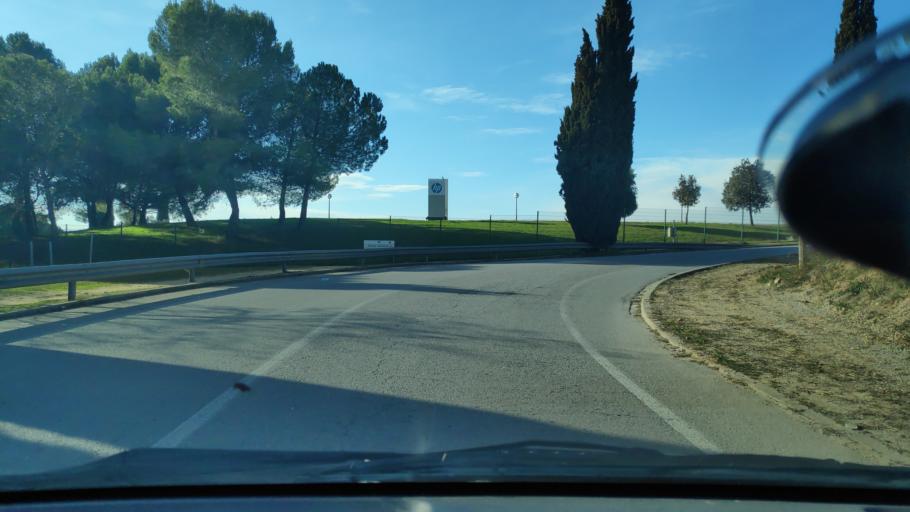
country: ES
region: Catalonia
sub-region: Provincia de Barcelona
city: Sant Cugat del Valles
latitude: 41.4909
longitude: 2.0668
